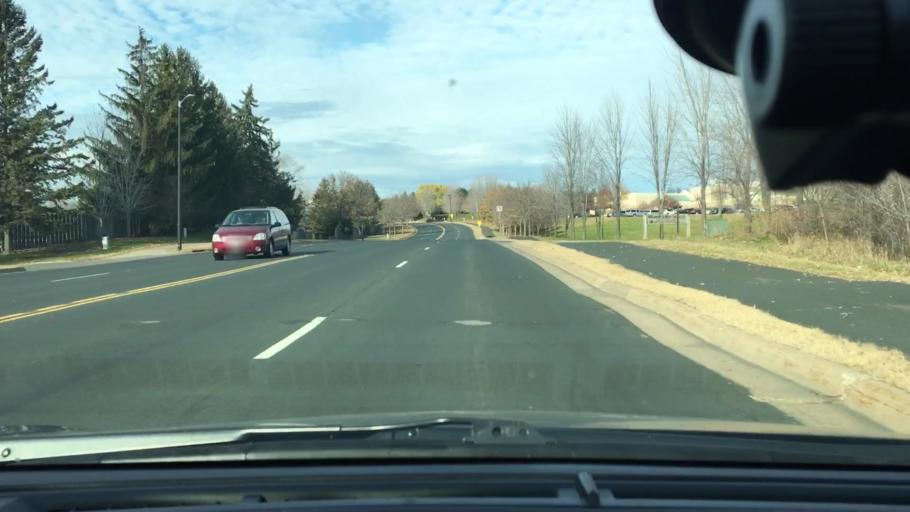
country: US
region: Minnesota
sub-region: Hennepin County
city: Maple Grove
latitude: 45.1078
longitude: -93.4824
